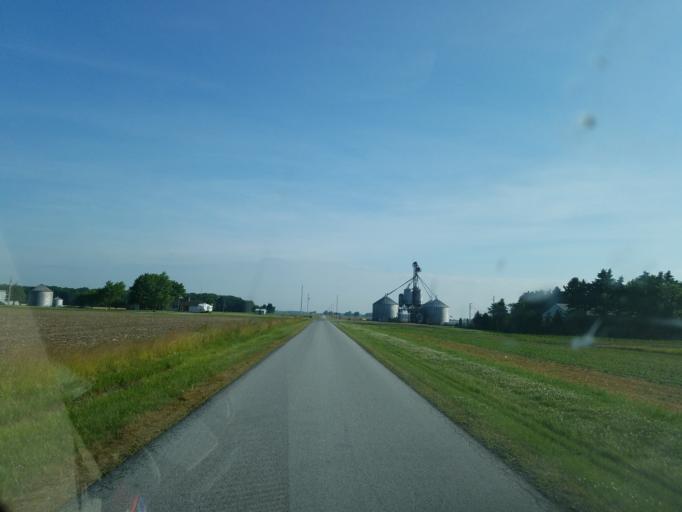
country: US
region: Ohio
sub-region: Hardin County
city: Kenton
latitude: 40.7452
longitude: -83.6716
